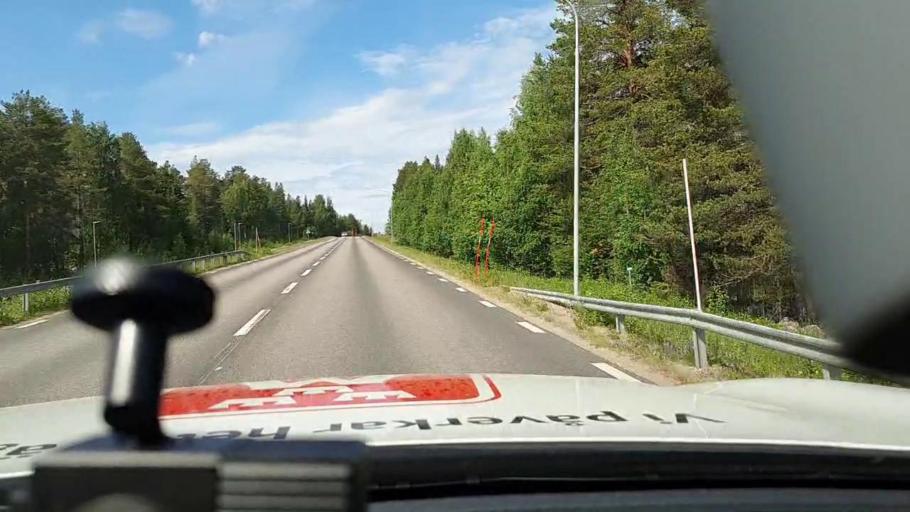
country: SE
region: Norrbotten
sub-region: Jokkmokks Kommun
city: Jokkmokk
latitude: 66.6028
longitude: 19.8591
